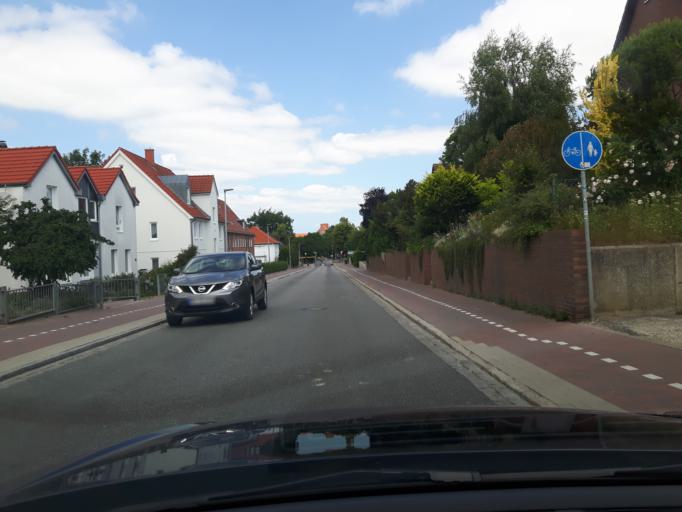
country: DE
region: Schleswig-Holstein
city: Neustadt in Holstein
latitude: 54.1039
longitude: 10.8211
